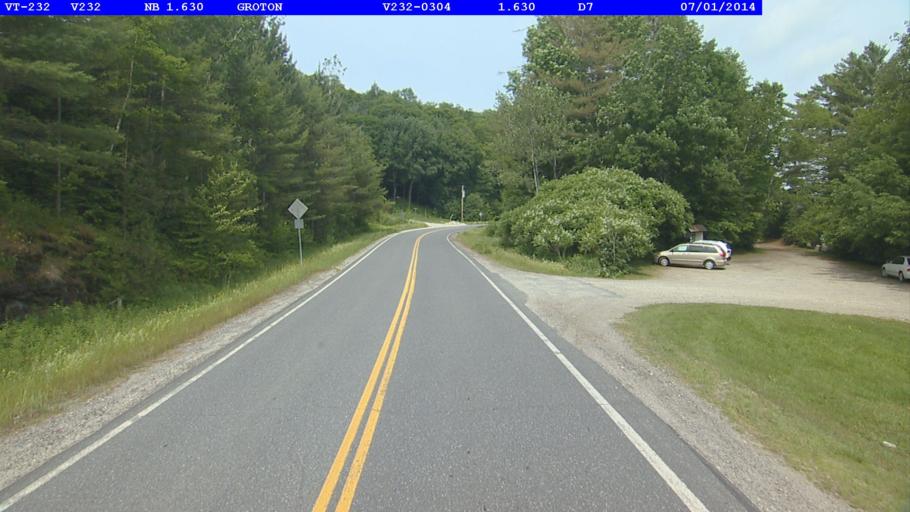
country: US
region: New Hampshire
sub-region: Grafton County
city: Woodsville
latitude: 44.2406
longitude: -72.2385
